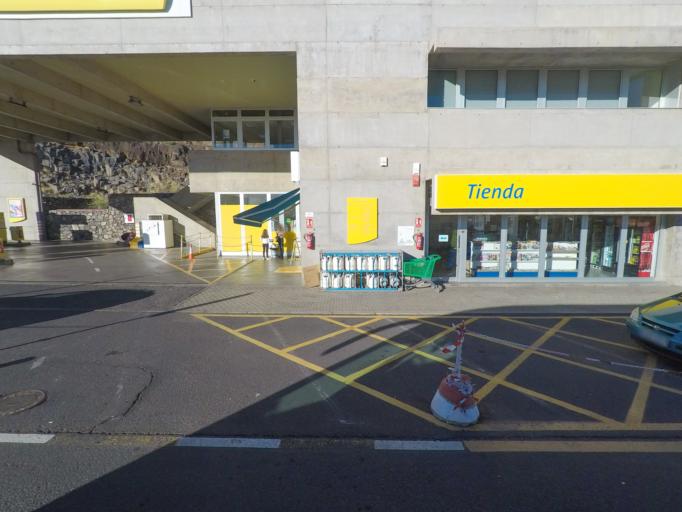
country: ES
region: Canary Islands
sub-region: Provincia de Santa Cruz de Tenerife
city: San Sebastian de la Gomera
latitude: 28.0895
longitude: -17.1074
